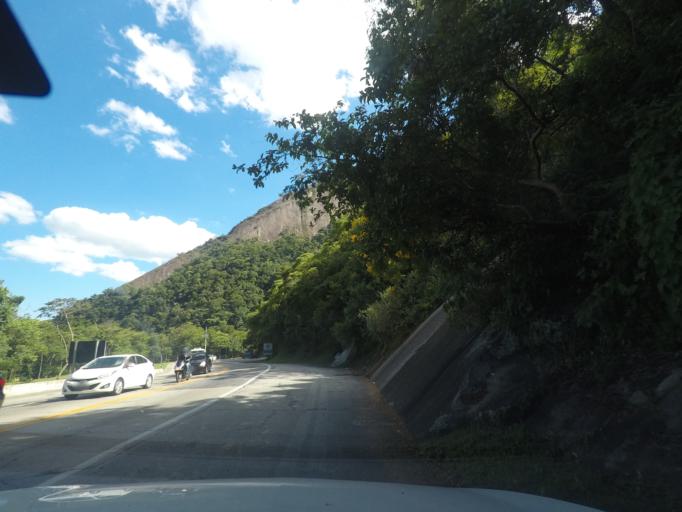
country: BR
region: Rio de Janeiro
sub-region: Teresopolis
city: Teresopolis
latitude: -22.4717
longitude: -43.0013
